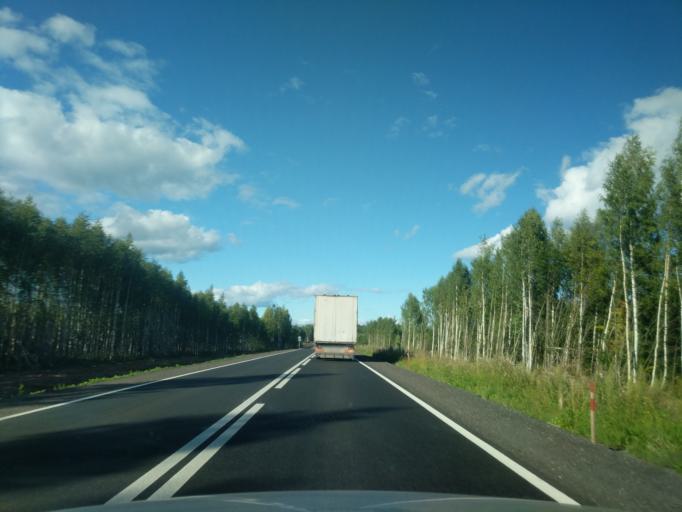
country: RU
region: Kostroma
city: Makar'yev
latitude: 57.9940
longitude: 43.9705
